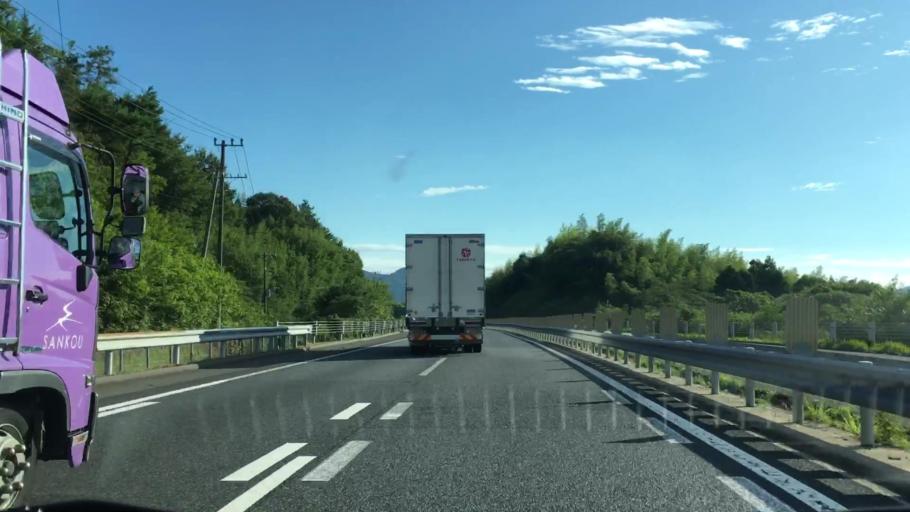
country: JP
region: Yamaguchi
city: Yanai
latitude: 34.0967
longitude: 132.0986
